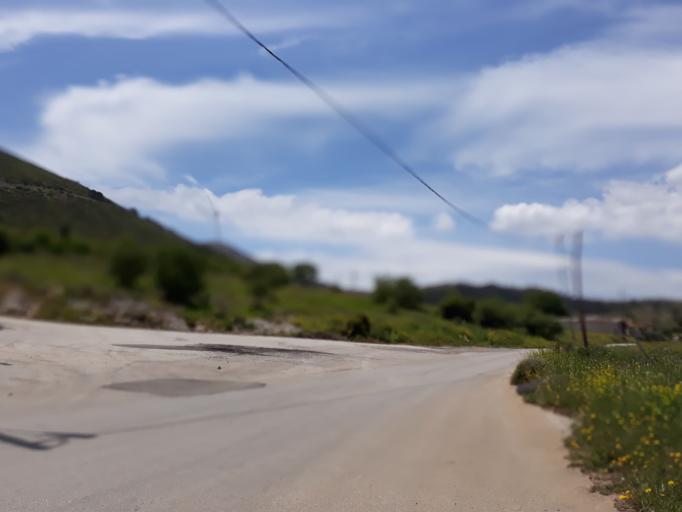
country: GR
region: Attica
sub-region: Nomarchia Dytikis Attikis
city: Magoula
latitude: 38.1791
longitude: 23.5502
